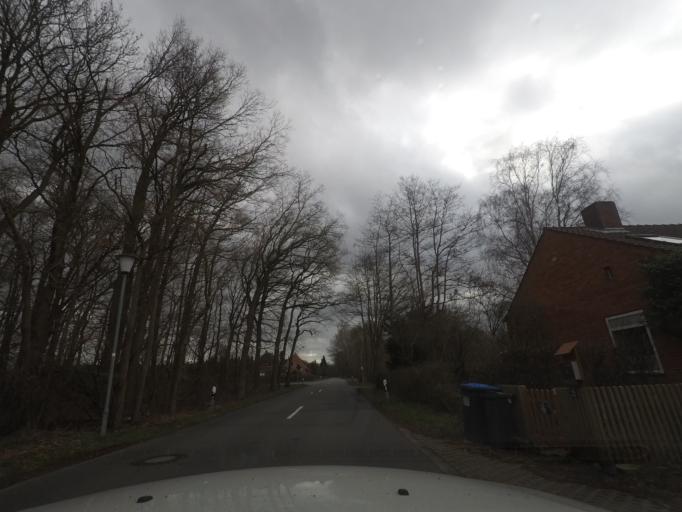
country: DE
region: Lower Saxony
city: Bad Bevensen
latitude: 53.0560
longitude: 10.6094
